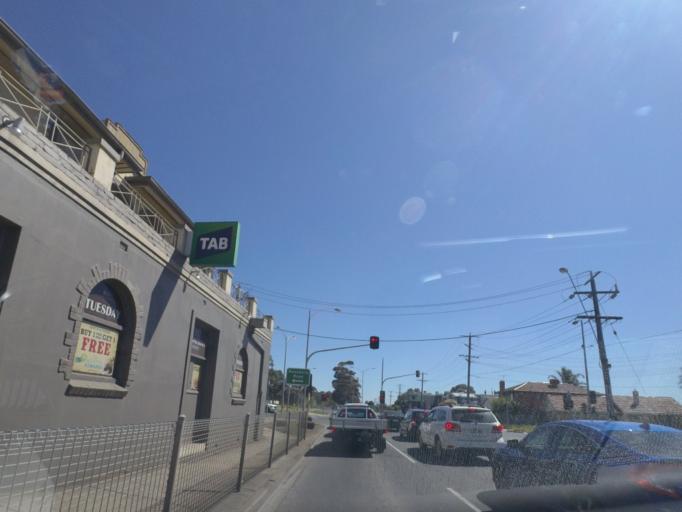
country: AU
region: Victoria
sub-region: Moreland
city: Fawkner
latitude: -37.7191
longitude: 144.9629
